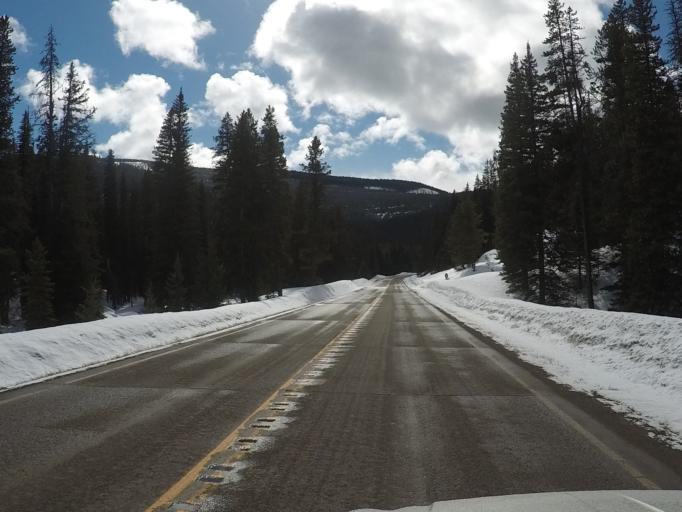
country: US
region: Montana
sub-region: Meagher County
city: White Sulphur Springs
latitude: 46.7622
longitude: -110.7153
